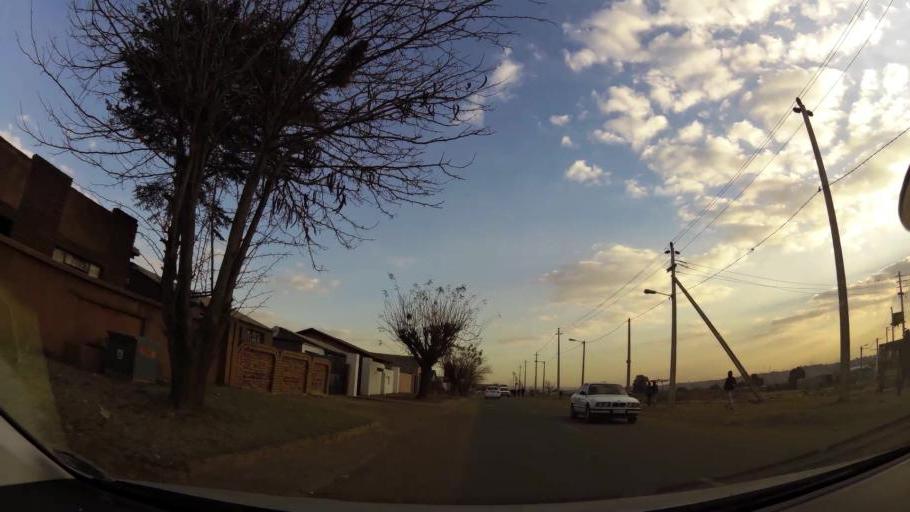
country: ZA
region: Gauteng
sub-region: City of Johannesburg Metropolitan Municipality
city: Soweto
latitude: -26.2661
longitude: 27.8956
